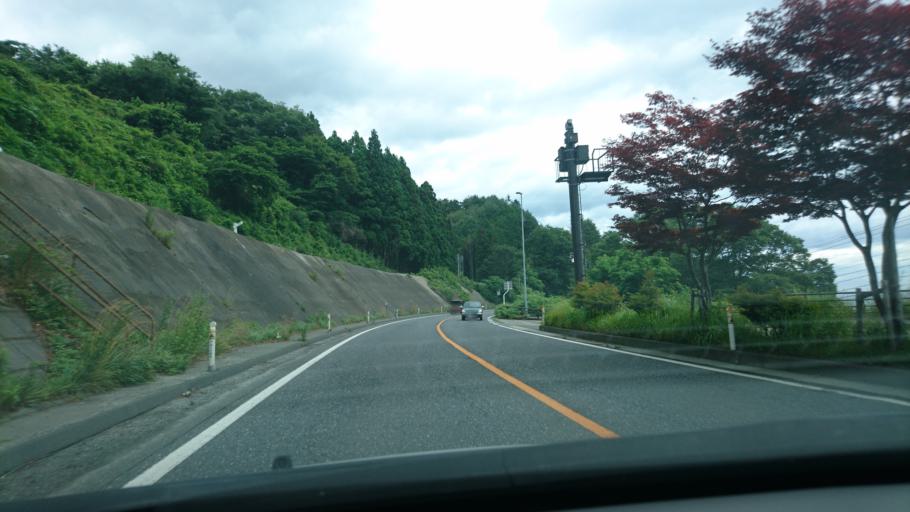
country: JP
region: Iwate
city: Otsuchi
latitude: 39.3877
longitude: 141.9390
